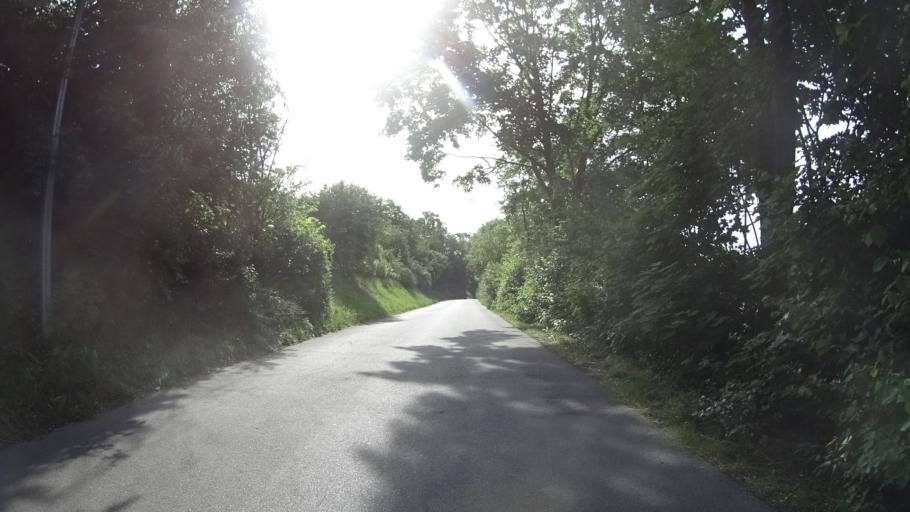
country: DE
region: Bavaria
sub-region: Lower Bavaria
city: Ihrlerstein
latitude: 48.9259
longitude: 11.8543
